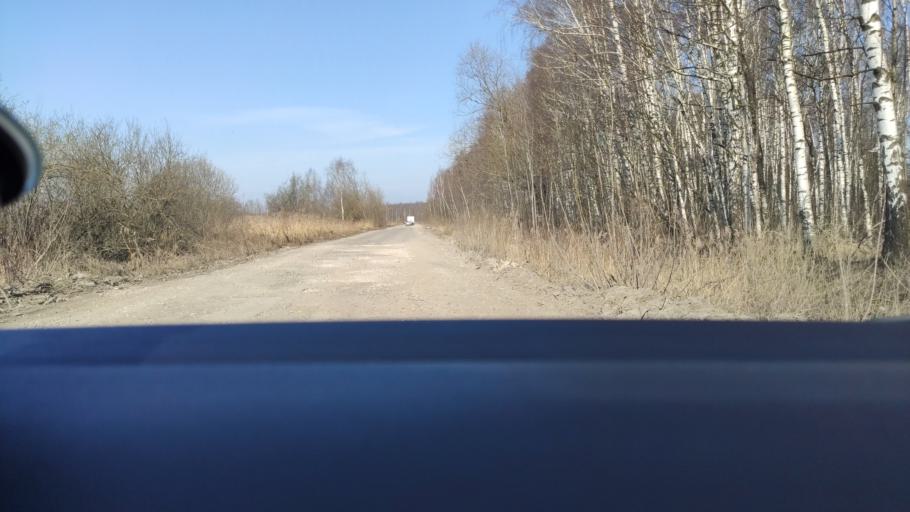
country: RU
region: Moskovskaya
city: Elektrostal'
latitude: 55.7685
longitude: 38.3852
